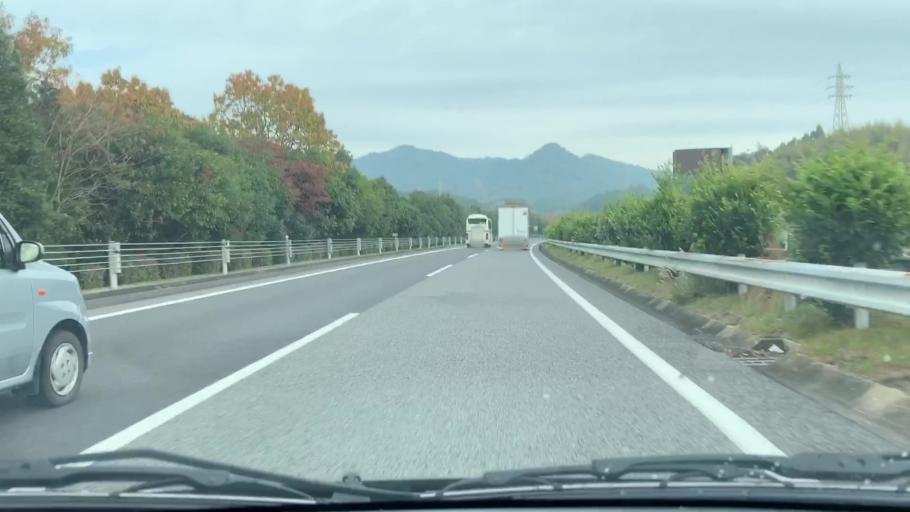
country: JP
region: Saga Prefecture
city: Takeocho-takeo
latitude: 33.2244
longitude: 130.0501
